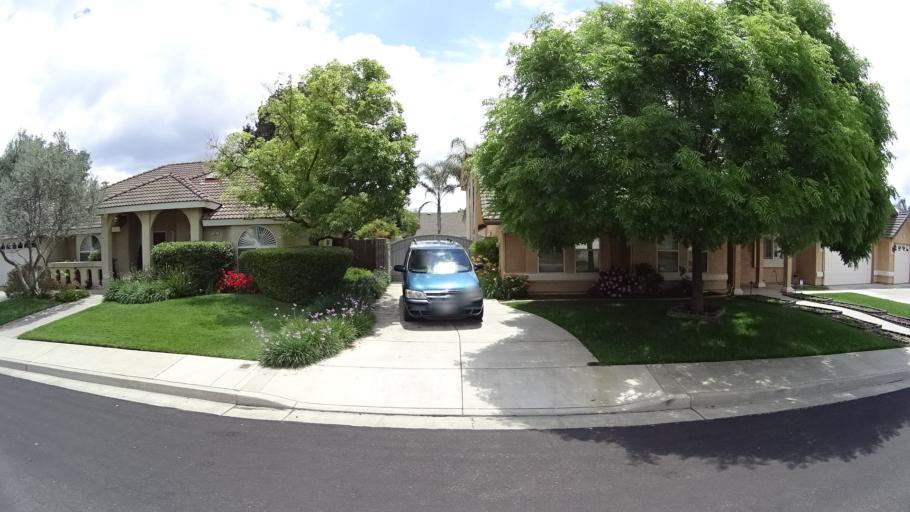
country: US
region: California
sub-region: Kings County
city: Hanford
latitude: 36.3532
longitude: -119.6522
